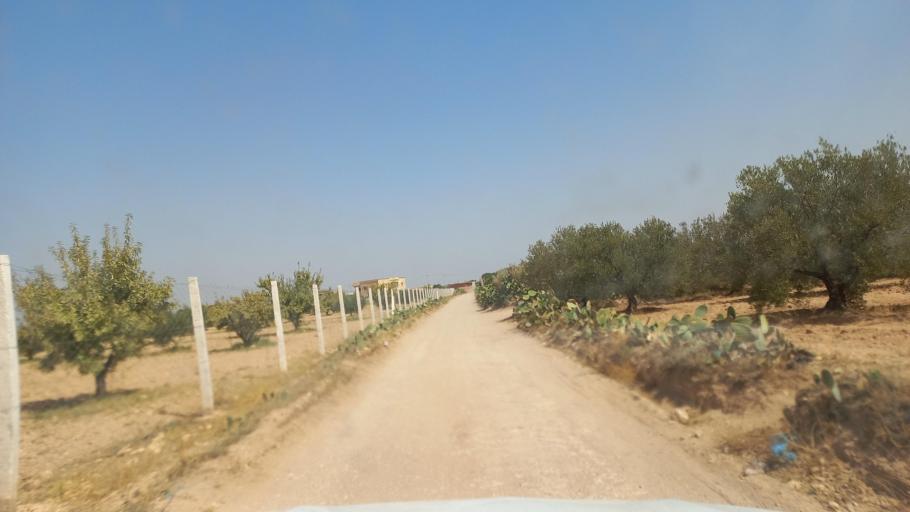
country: TN
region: Al Qasrayn
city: Kasserine
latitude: 35.2488
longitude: 9.0195
